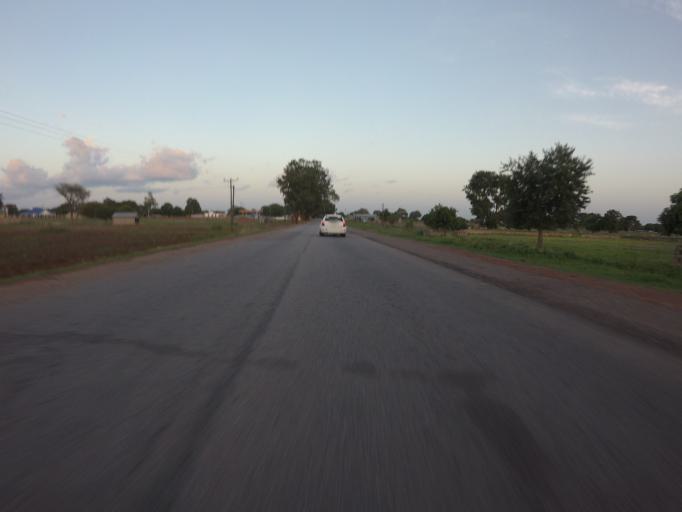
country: GH
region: Upper East
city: Navrongo
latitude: 10.8576
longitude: -1.0277
